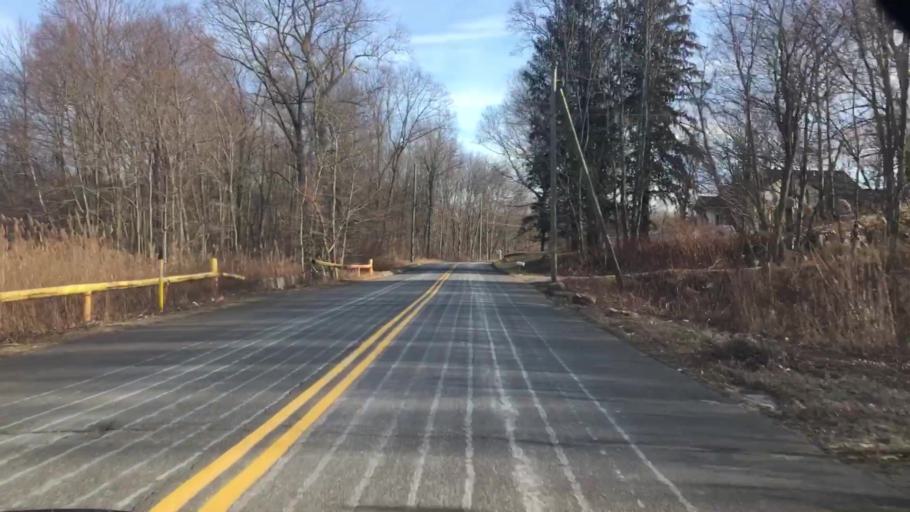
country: US
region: Connecticut
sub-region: New Haven County
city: Prospect
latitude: 41.5328
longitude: -72.9645
